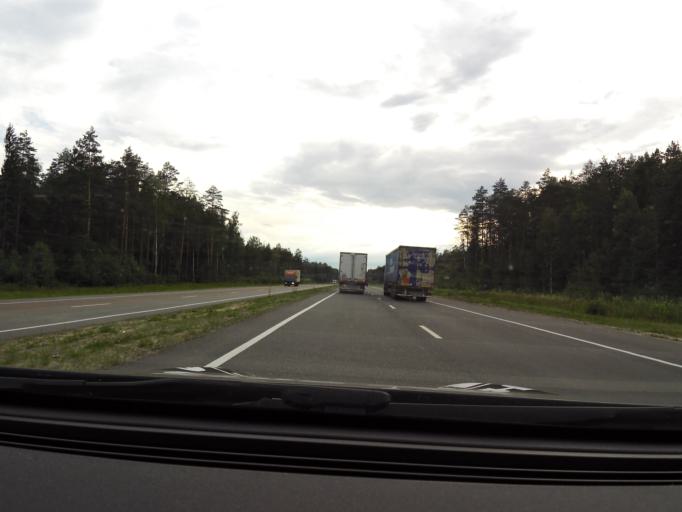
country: RU
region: Vladimir
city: Kommunar
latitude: 56.0936
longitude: 40.5400
